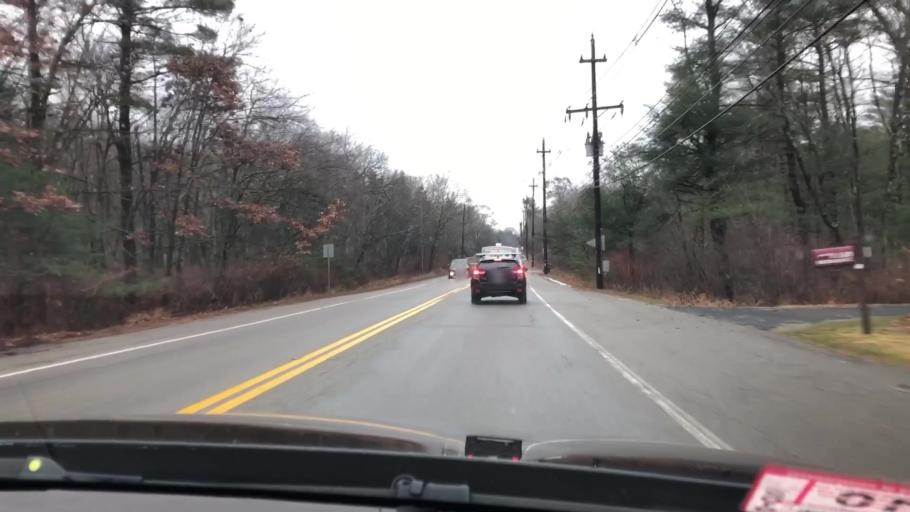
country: US
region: Massachusetts
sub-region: Norfolk County
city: Wrentham
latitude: 42.0711
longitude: -71.3224
